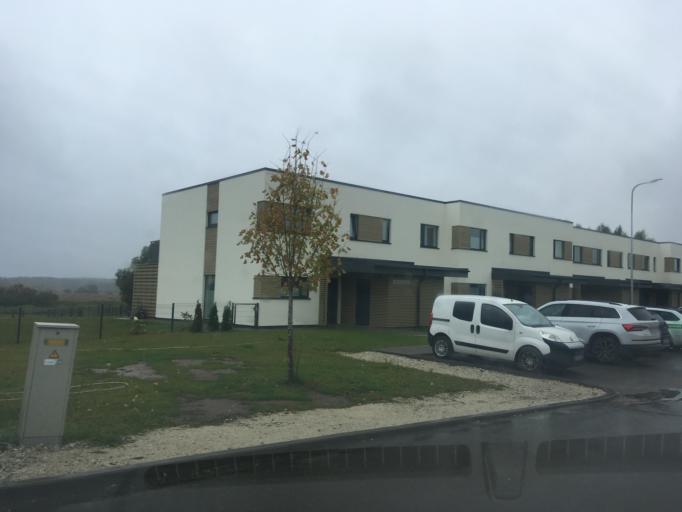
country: EE
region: Tartu
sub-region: UElenurme vald
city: Ulenurme
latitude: 58.3381
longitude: 26.7886
